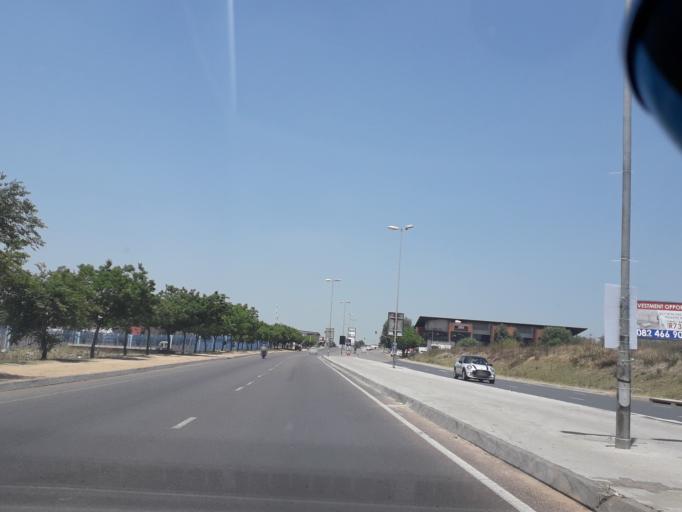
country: ZA
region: Gauteng
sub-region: City of Johannesburg Metropolitan Municipality
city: Midrand
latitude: -25.9739
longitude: 28.1197
